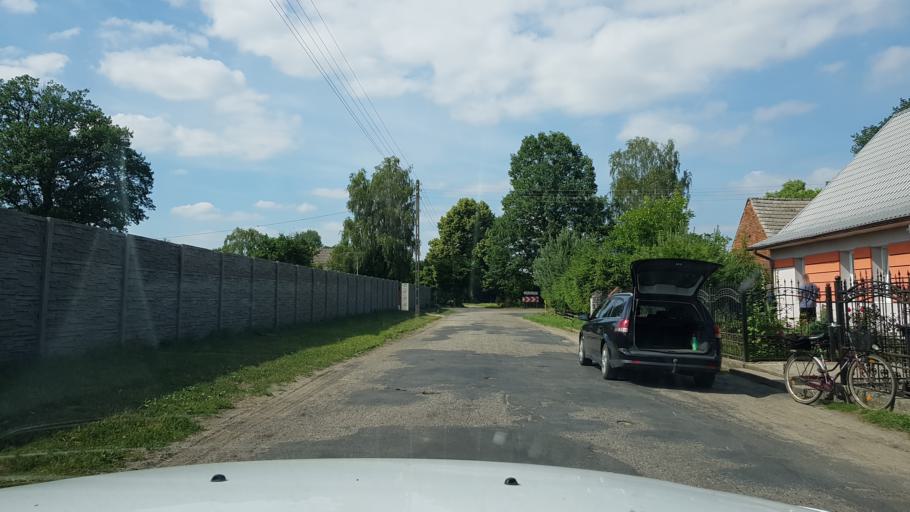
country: PL
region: West Pomeranian Voivodeship
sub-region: Powiat goleniowski
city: Mosty
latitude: 53.5776
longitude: 14.9780
